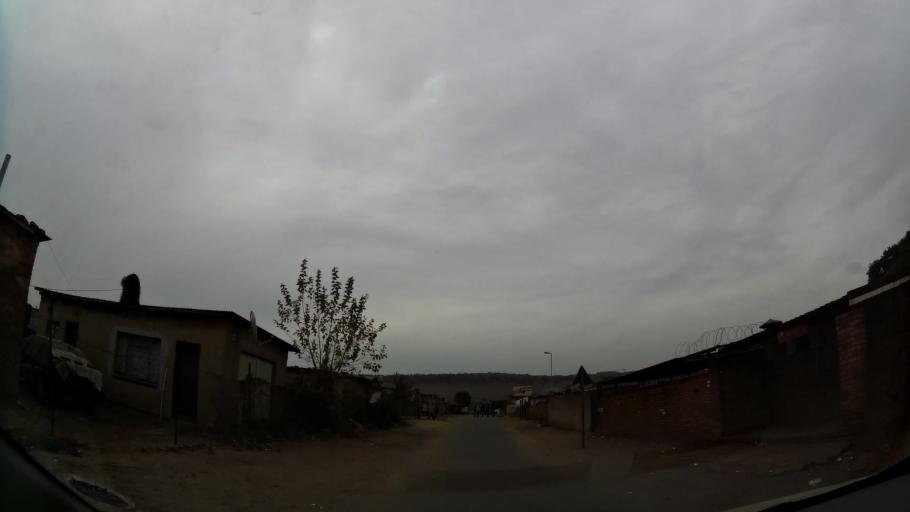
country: ZA
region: Gauteng
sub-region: City of Tshwane Metropolitan Municipality
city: Pretoria
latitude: -25.7080
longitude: 28.3338
